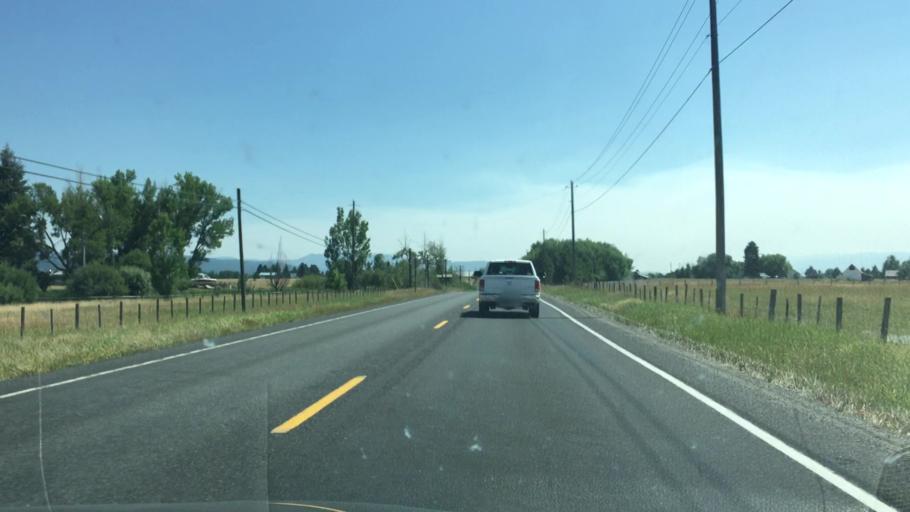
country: US
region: Idaho
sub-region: Valley County
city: McCall
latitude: 44.8452
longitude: -116.0889
